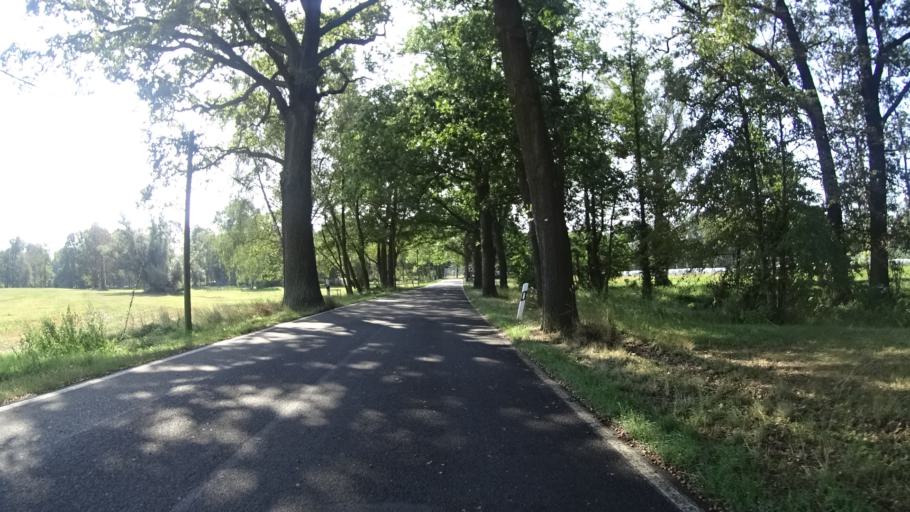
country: DE
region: Brandenburg
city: Burg
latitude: 51.8504
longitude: 14.1367
